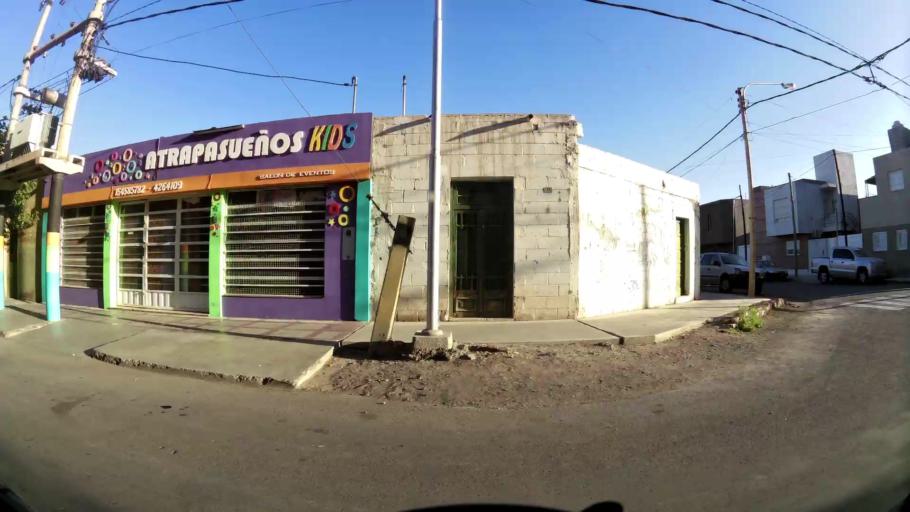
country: AR
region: San Juan
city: San Juan
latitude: -31.5447
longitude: -68.5208
